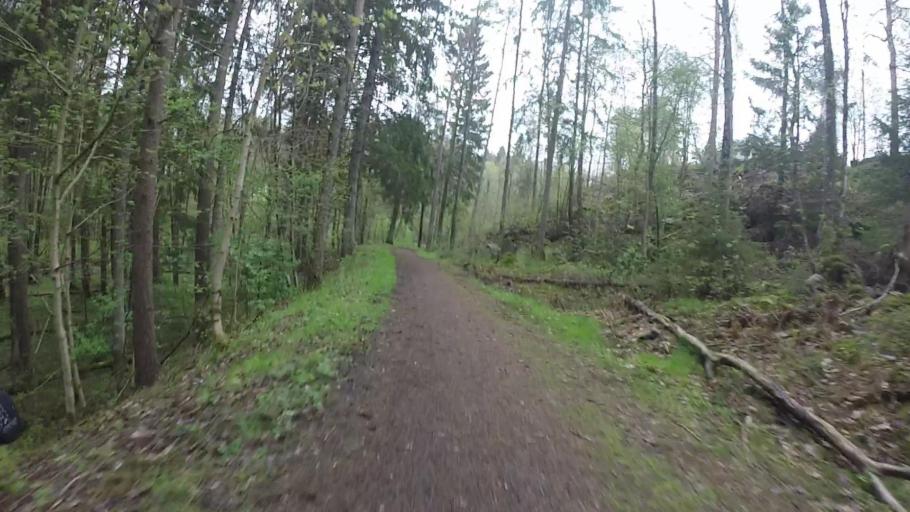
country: SE
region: Vaestra Goetaland
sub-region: Trollhattan
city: Trollhattan
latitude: 58.2602
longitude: 12.2543
